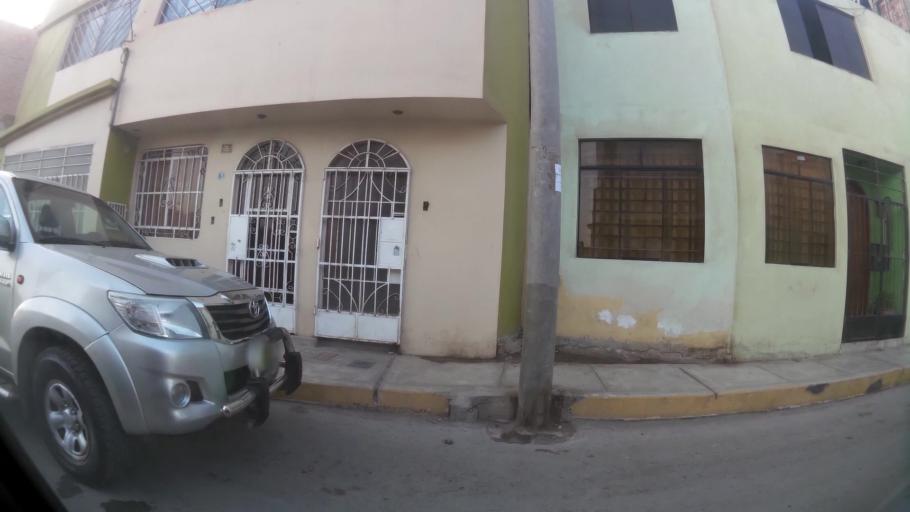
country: PE
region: Lima
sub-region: Huaura
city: Huacho
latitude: -11.1176
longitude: -77.6081
